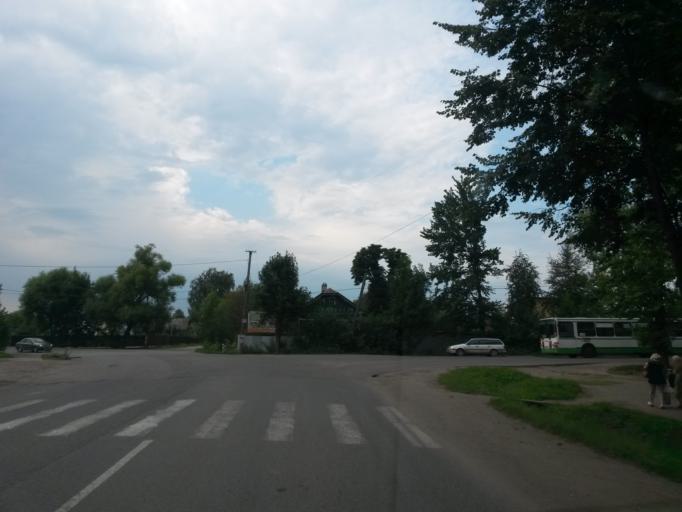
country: RU
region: Jaroslavl
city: Yaroslavl
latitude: 57.6074
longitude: 39.8135
